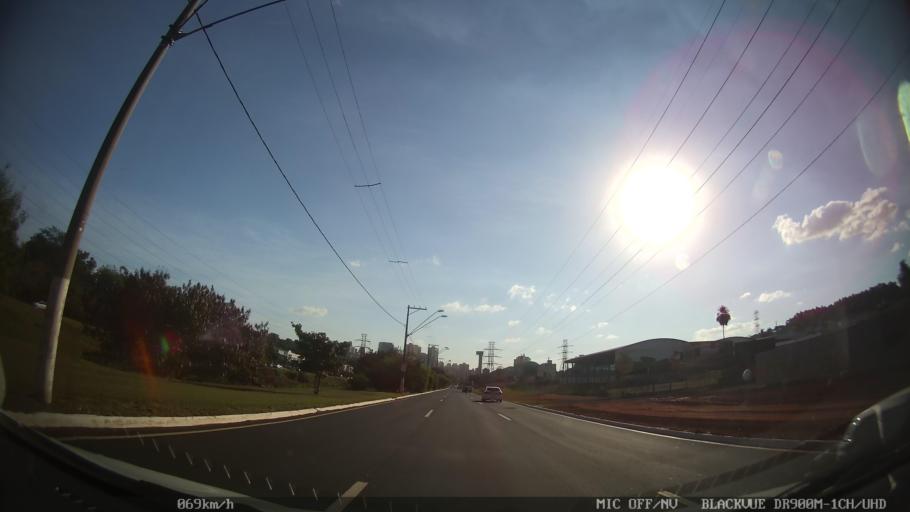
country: BR
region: Sao Paulo
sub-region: Ribeirao Preto
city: Ribeirao Preto
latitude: -21.2100
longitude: -47.7819
